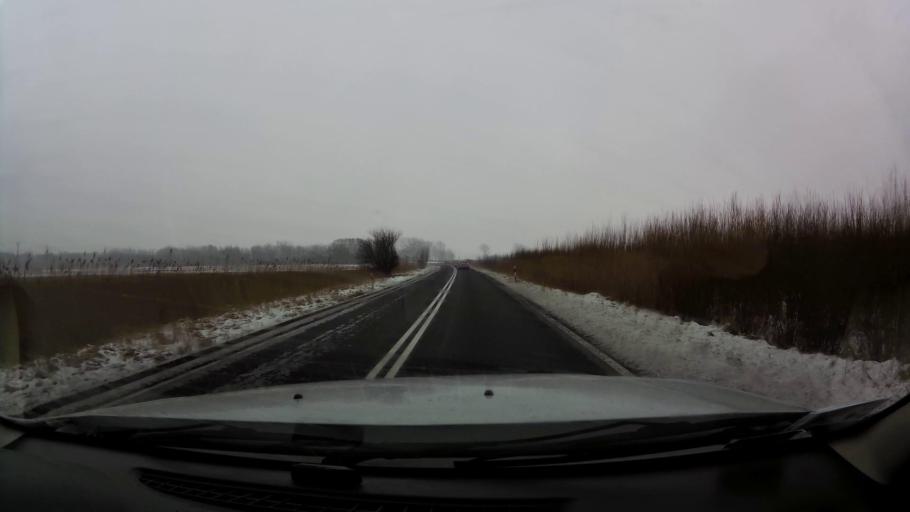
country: PL
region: West Pomeranian Voivodeship
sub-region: Powiat gryficki
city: Mrzezyno
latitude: 54.1105
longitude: 15.2655
